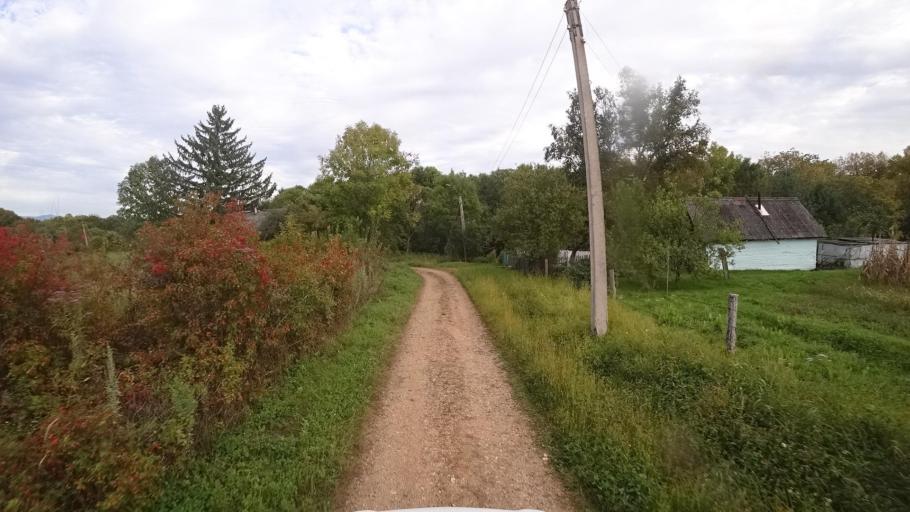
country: RU
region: Primorskiy
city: Dostoyevka
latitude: 44.3447
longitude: 133.4084
